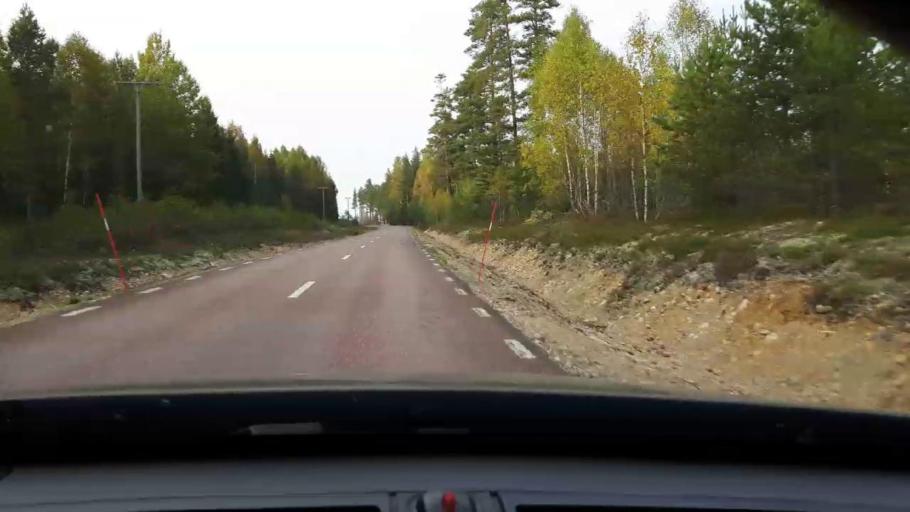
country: SE
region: Dalarna
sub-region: Gagnefs Kommun
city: Mockfjard
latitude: 60.3080
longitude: 14.9446
